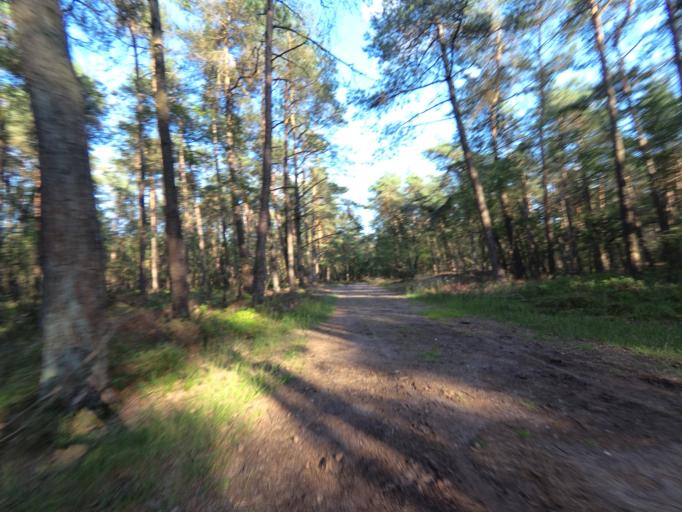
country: NL
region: Gelderland
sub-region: Gemeente Apeldoorn
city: Beekbergen
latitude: 52.1391
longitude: 5.9000
